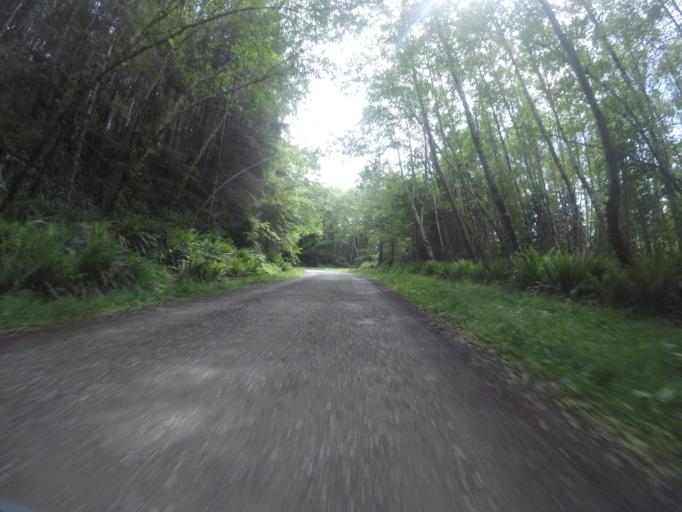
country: US
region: California
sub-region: Humboldt County
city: Westhaven-Moonstone
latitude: 41.2242
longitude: -124.0031
